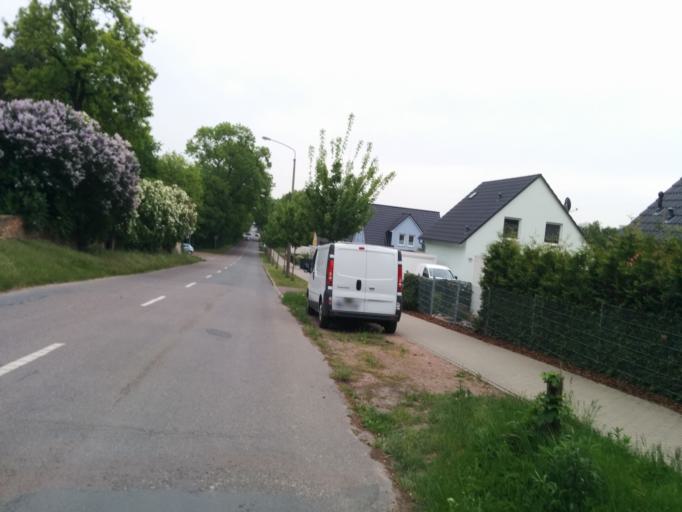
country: DE
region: Saxony-Anhalt
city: Zscherben
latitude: 51.4814
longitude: 11.8866
